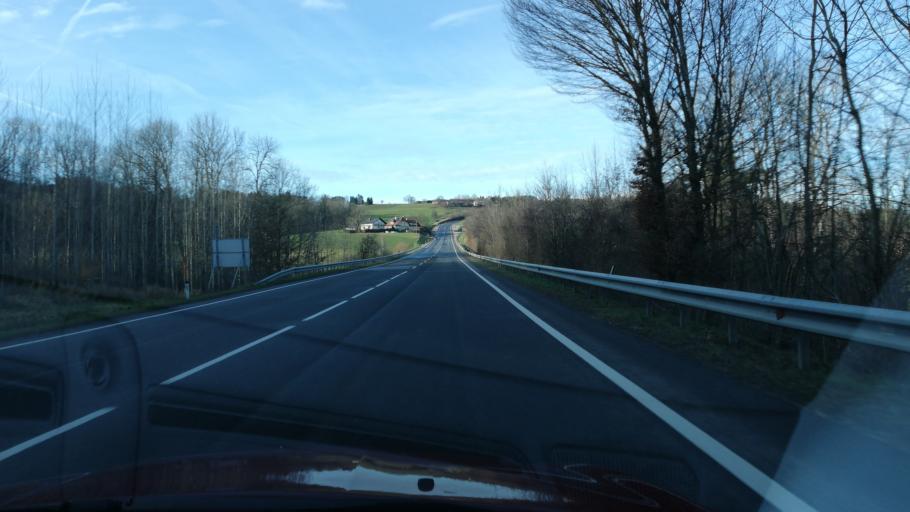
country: AT
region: Upper Austria
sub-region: Politischer Bezirk Kirchdorf an der Krems
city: Micheldorf in Oberoesterreich
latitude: 47.9525
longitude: 14.0909
